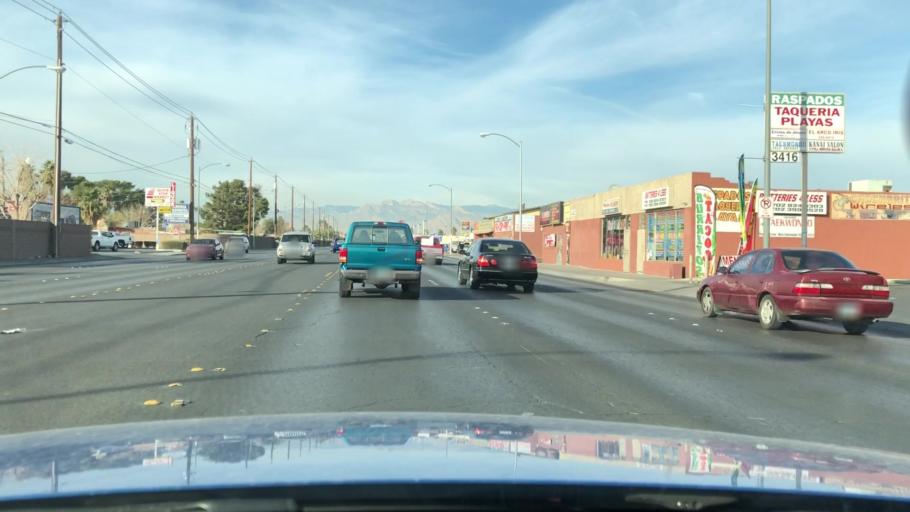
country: US
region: Nevada
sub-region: Clark County
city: North Las Vegas
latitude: 36.1959
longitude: -115.1019
